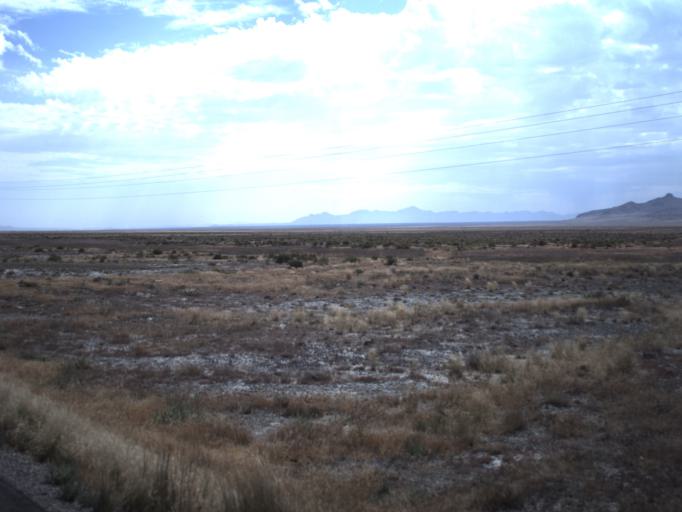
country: US
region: Utah
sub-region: Tooele County
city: Wendover
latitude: 41.4268
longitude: -113.8391
